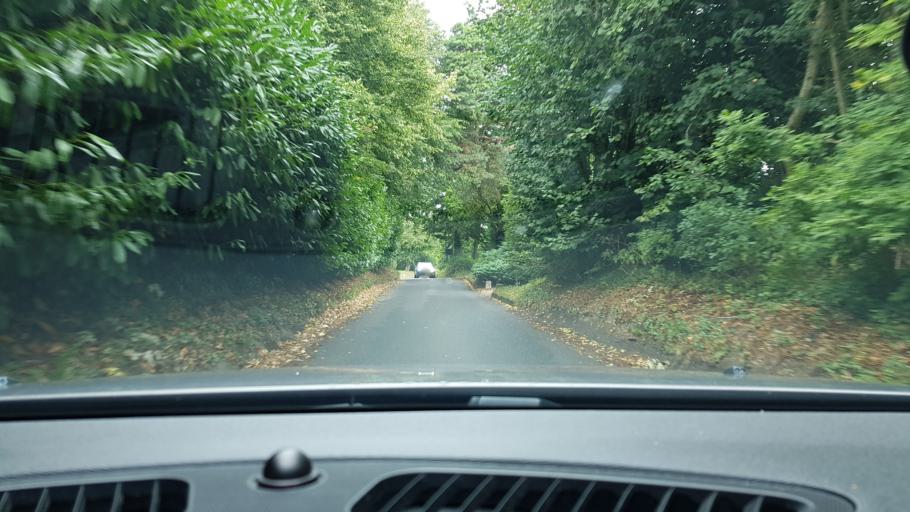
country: GB
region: England
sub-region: Wiltshire
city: Shalbourne
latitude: 51.3671
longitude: -1.5282
